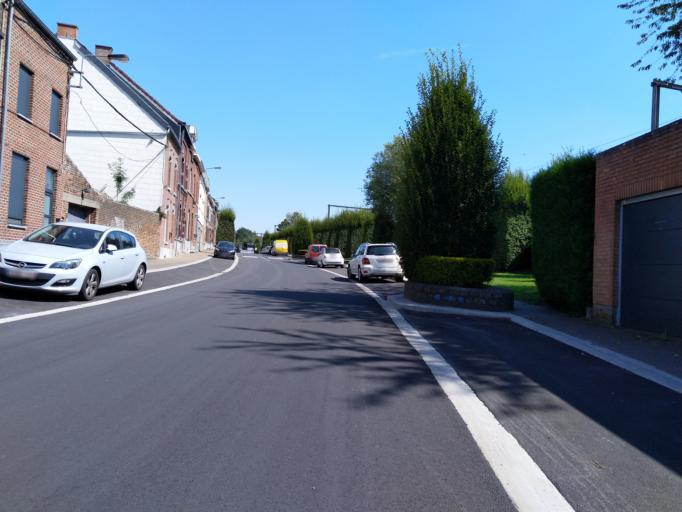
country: BE
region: Wallonia
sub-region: Province du Hainaut
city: Roeulx
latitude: 50.4732
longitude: 4.1176
